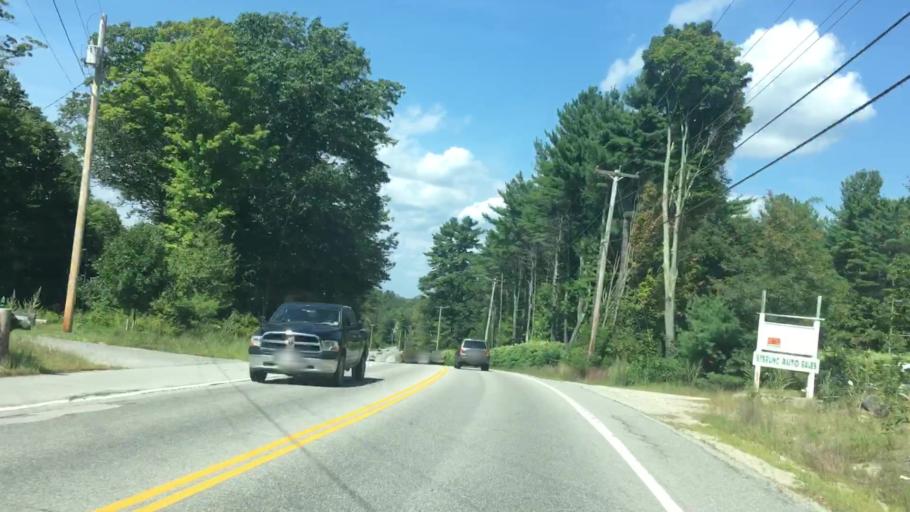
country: US
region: Maine
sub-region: Cumberland County
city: New Gloucester
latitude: 43.9045
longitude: -70.3233
